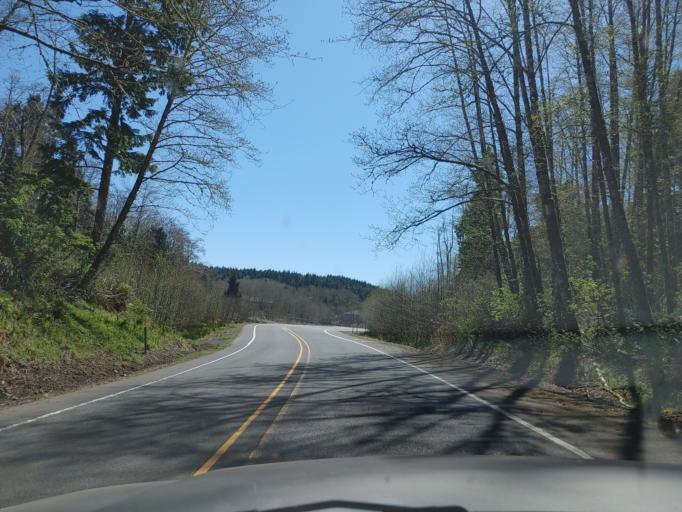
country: US
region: Oregon
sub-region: Clatsop County
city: Warrenton
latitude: 46.1462
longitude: -123.9021
